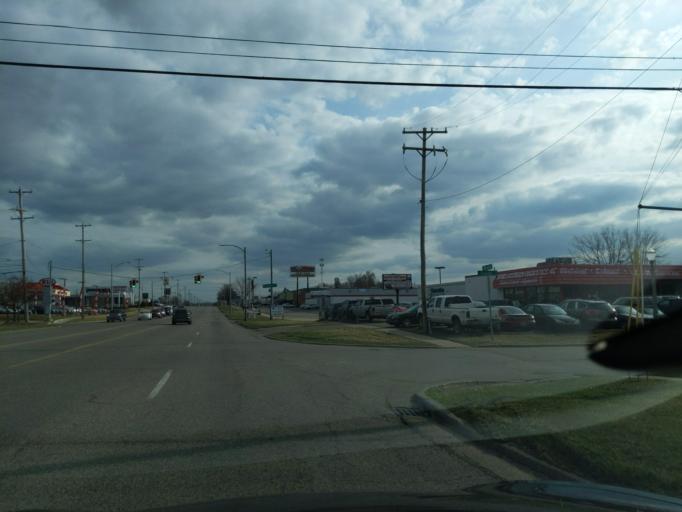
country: US
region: Michigan
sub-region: Ingham County
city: Holt
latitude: 42.6753
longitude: -84.5382
